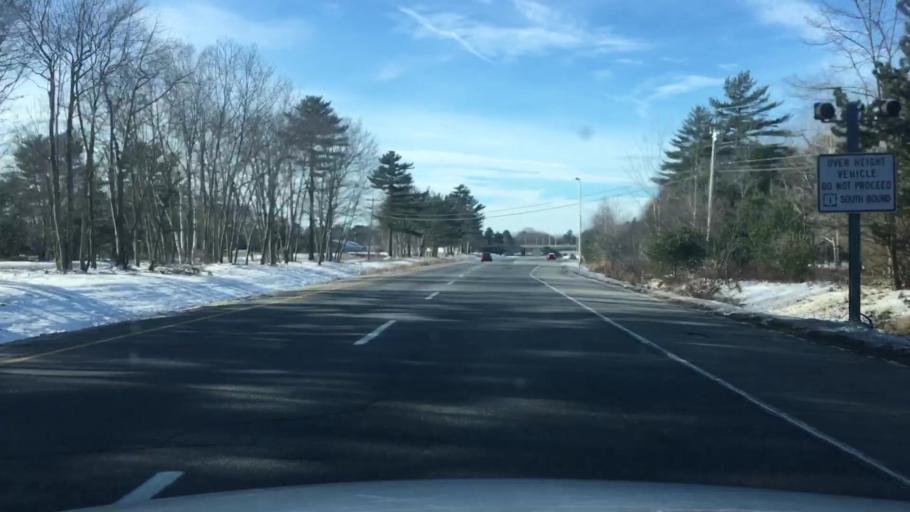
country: US
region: Maine
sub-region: Cumberland County
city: Brunswick
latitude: 43.9119
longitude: -69.9095
